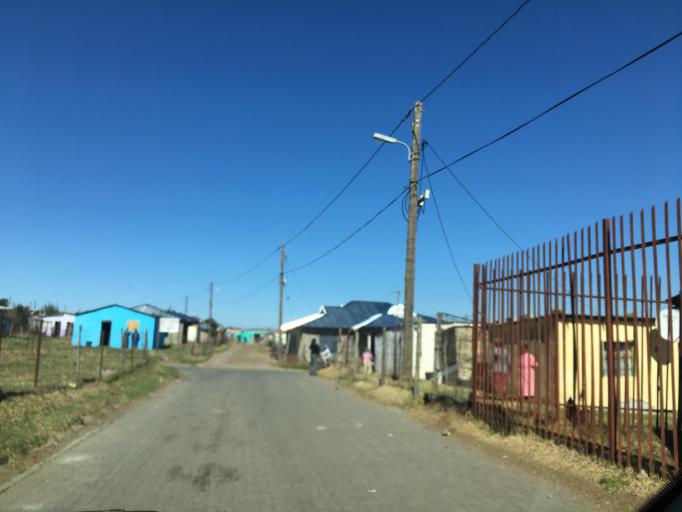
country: ZA
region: Eastern Cape
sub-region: Chris Hani District Municipality
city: Elliot
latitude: -31.3354
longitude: 27.8597
